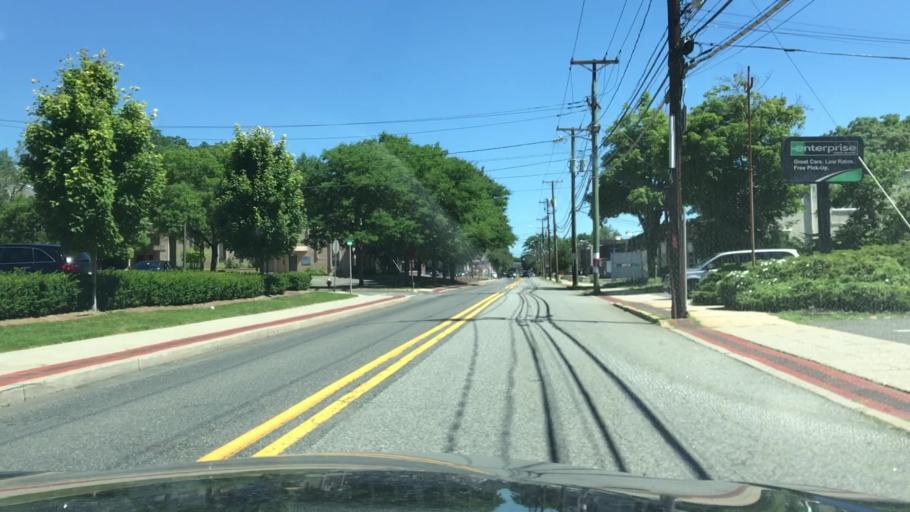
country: US
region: New Jersey
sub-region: Bergen County
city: Ho-Ho-Kus
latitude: 40.9937
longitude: -74.1113
